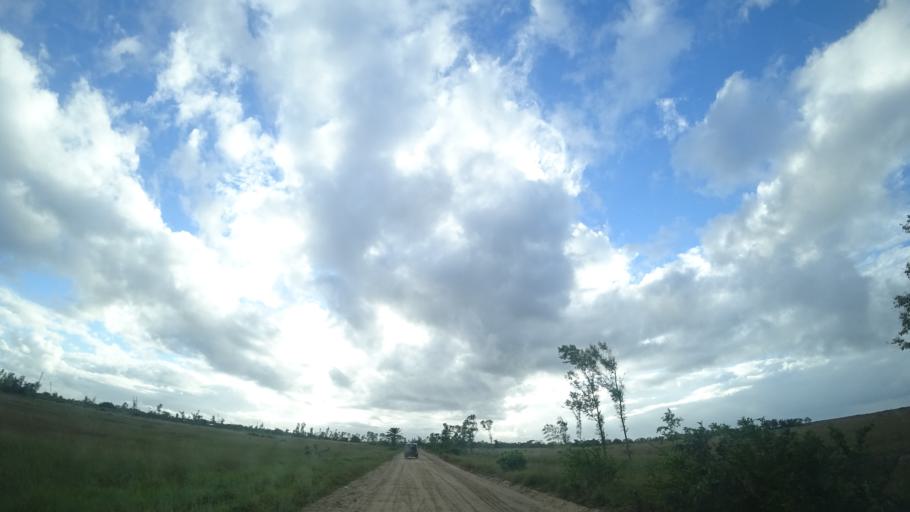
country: MZ
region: Sofala
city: Beira
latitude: -19.7229
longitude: 34.9959
